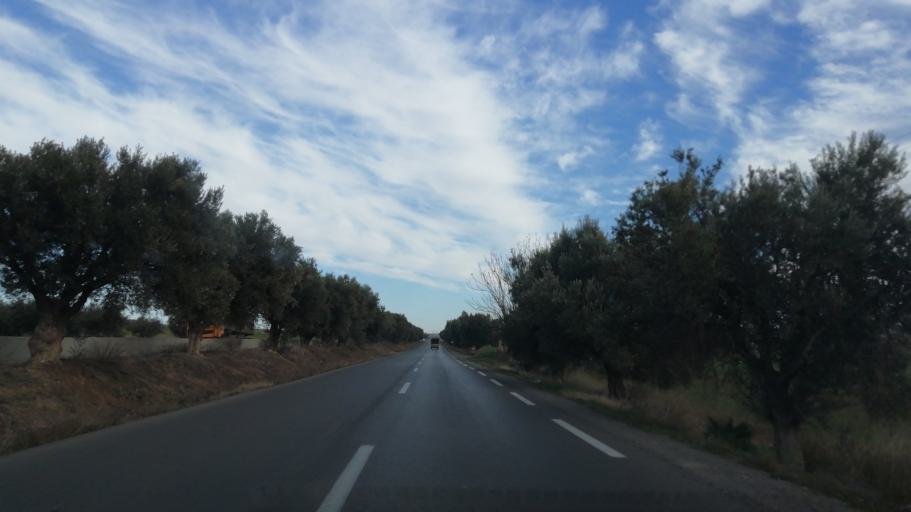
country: DZ
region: Sidi Bel Abbes
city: Sfizef
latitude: 35.1783
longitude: -0.4329
